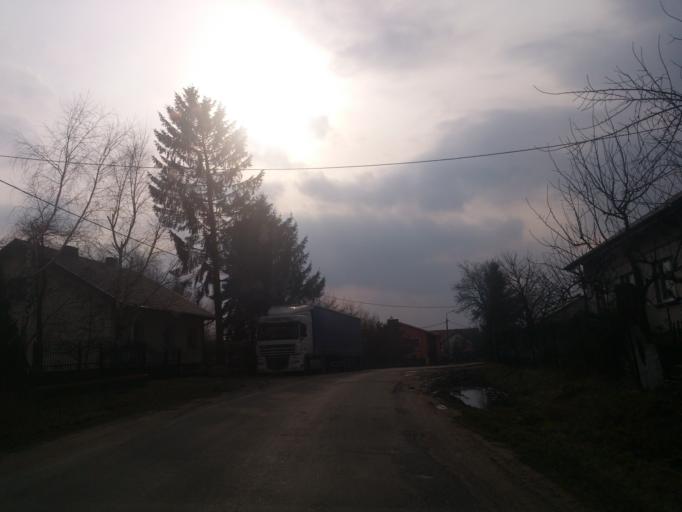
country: PL
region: Kujawsko-Pomorskie
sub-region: Powiat golubsko-dobrzynski
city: Golub-Dobrzyn
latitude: 53.0669
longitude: 19.0695
